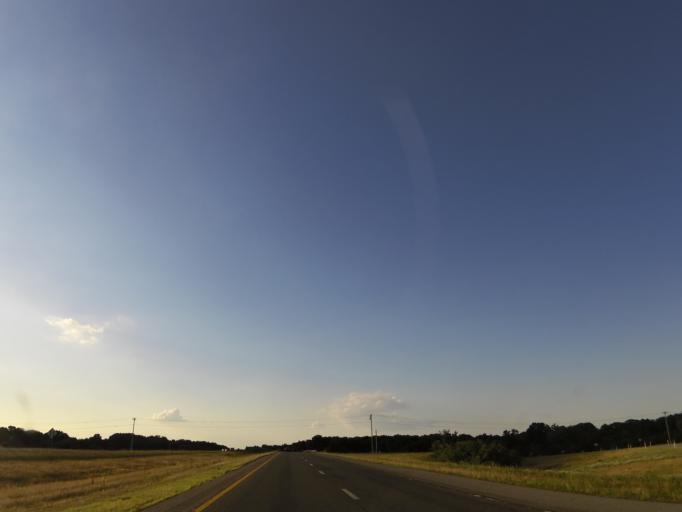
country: US
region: Tennessee
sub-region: Rutherford County
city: Smyrna
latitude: 35.9364
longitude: -86.4362
